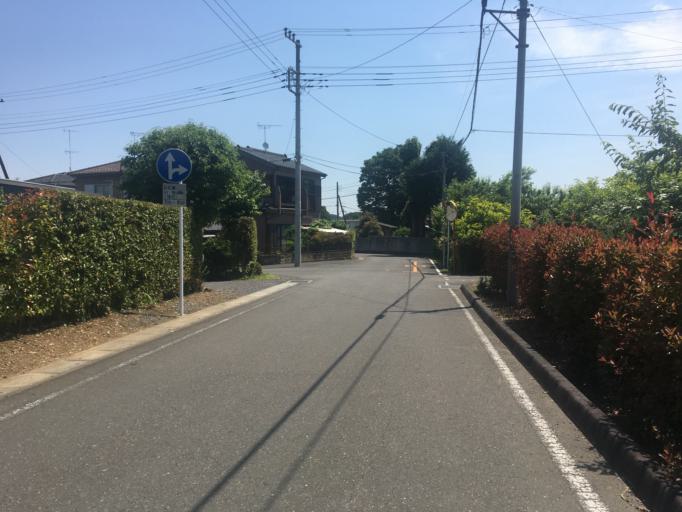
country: JP
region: Saitama
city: Ogawa
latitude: 36.0021
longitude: 139.2767
